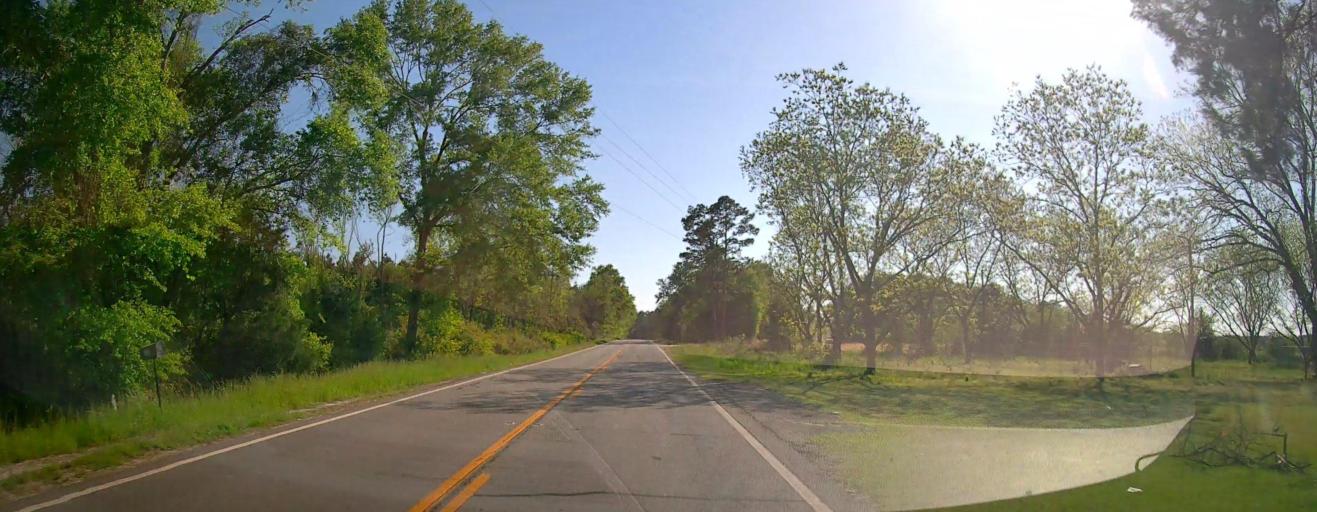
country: US
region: Georgia
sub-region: Wilcox County
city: Rochelle
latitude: 31.9047
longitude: -83.4837
